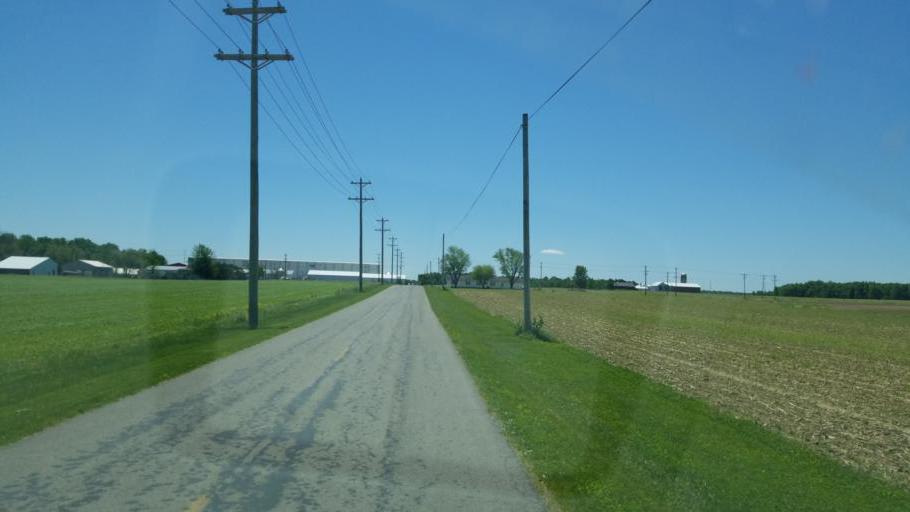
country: US
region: Ohio
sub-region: Mercer County
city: Fort Recovery
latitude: 40.3696
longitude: -84.7290
